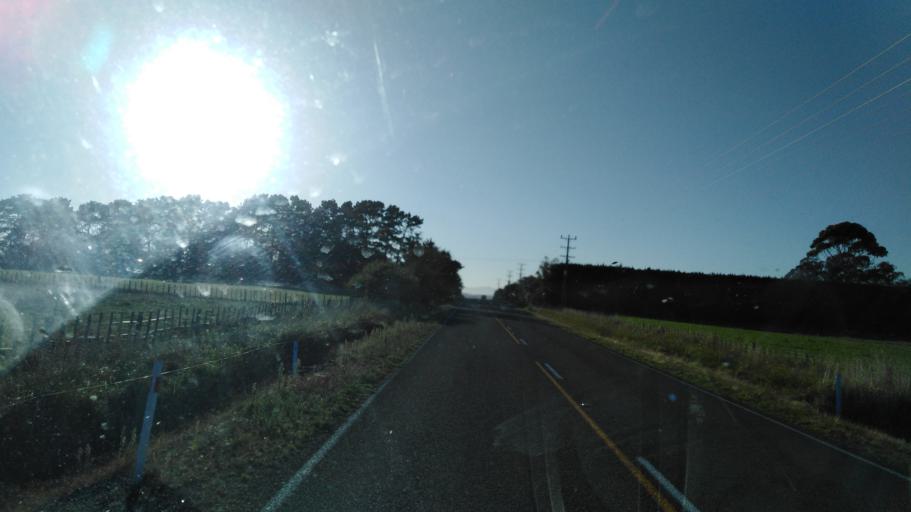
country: NZ
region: Manawatu-Wanganui
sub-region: Rangitikei District
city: Bulls
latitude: -40.0692
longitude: 175.4127
